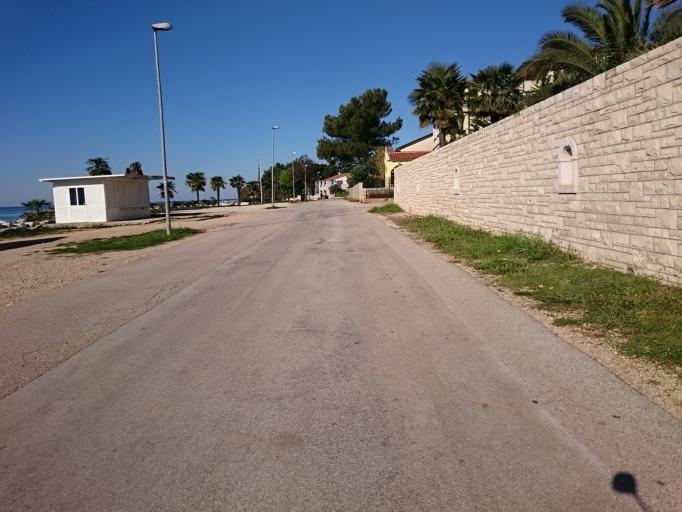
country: HR
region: Istarska
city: Umag
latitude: 45.3805
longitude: 13.5421
